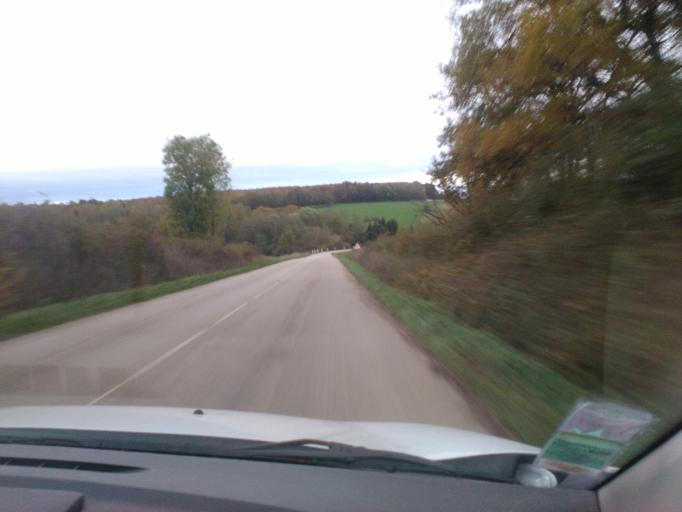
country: FR
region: Lorraine
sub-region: Departement des Vosges
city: Darnieulles
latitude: 48.2473
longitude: 6.3451
